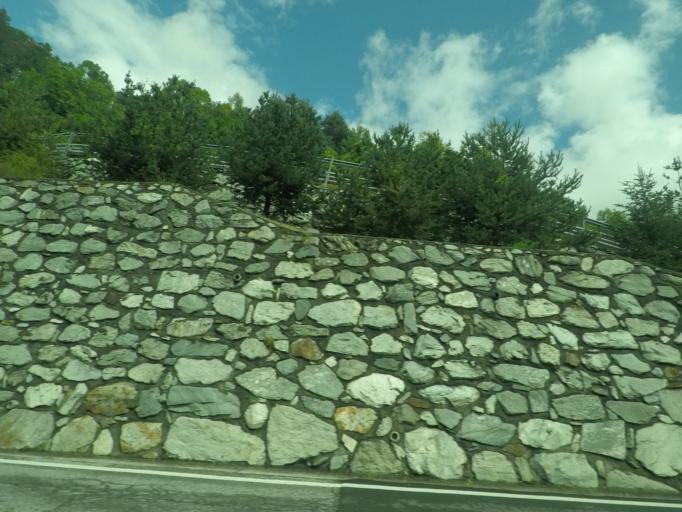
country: IT
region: Aosta Valley
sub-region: Valle d'Aosta
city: Antey-Saint-Andre
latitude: 45.7964
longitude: 7.5914
